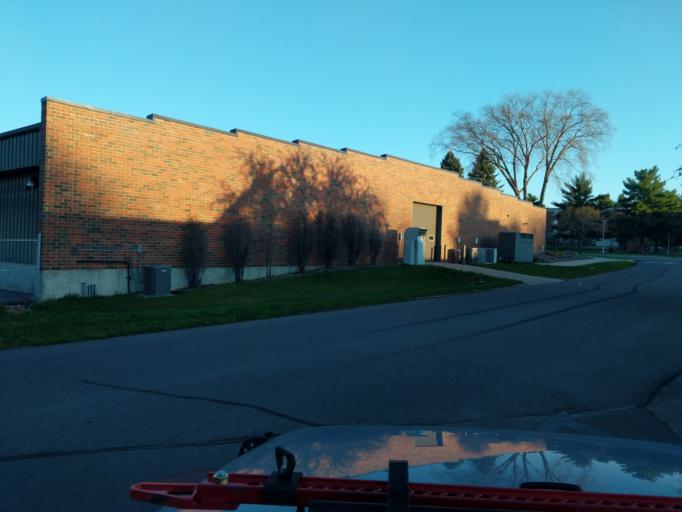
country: US
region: Wisconsin
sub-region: Pierce County
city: River Falls
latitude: 44.8516
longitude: -92.6166
